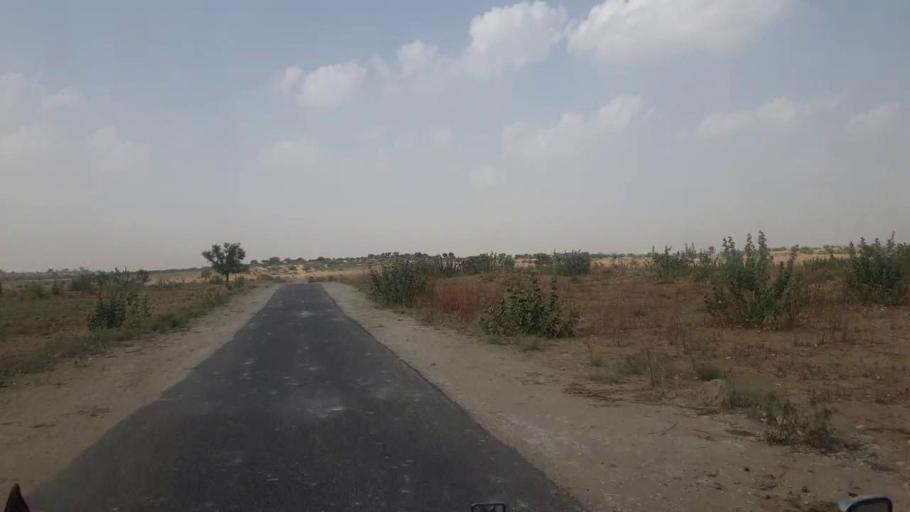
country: PK
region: Sindh
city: Islamkot
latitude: 25.2278
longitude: 70.2866
